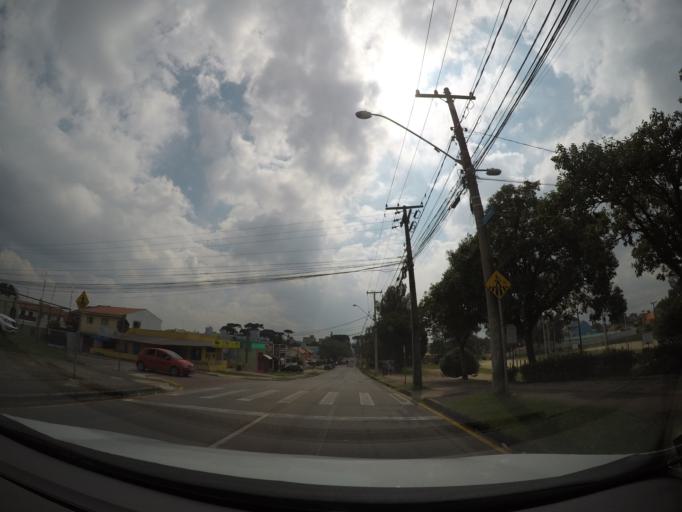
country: BR
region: Parana
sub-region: Sao Jose Dos Pinhais
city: Sao Jose dos Pinhais
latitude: -25.5056
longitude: -49.2480
